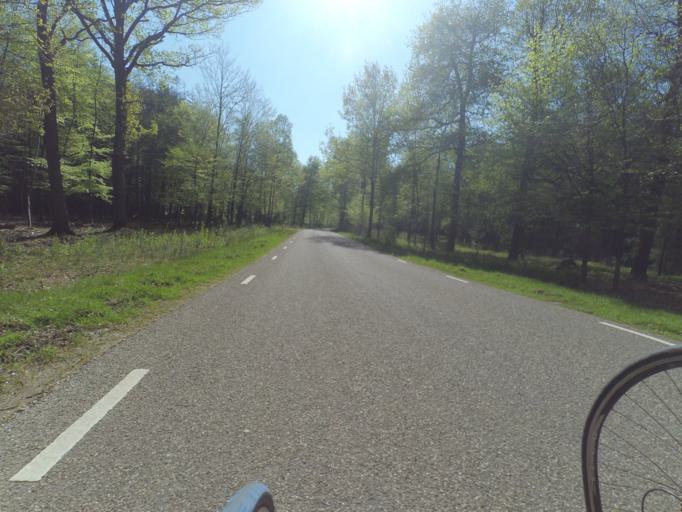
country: NL
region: Gelderland
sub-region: Gemeente Apeldoorn
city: Uddel
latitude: 52.2314
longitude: 5.8647
